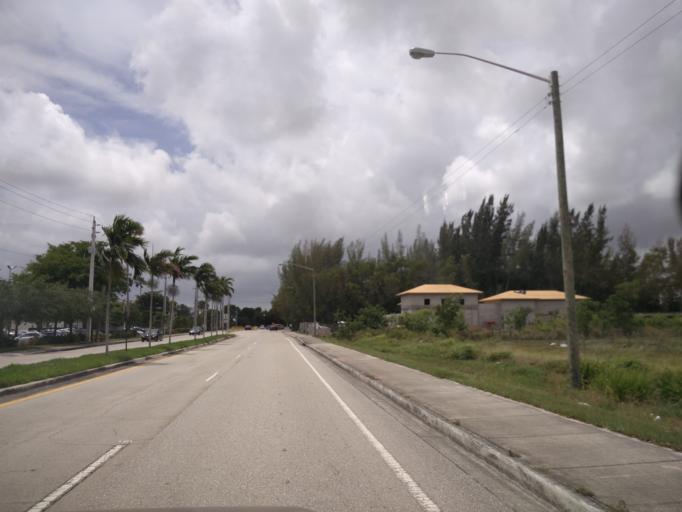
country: US
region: Florida
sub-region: Palm Beach County
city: Villages of Oriole
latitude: 26.4563
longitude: -80.1634
